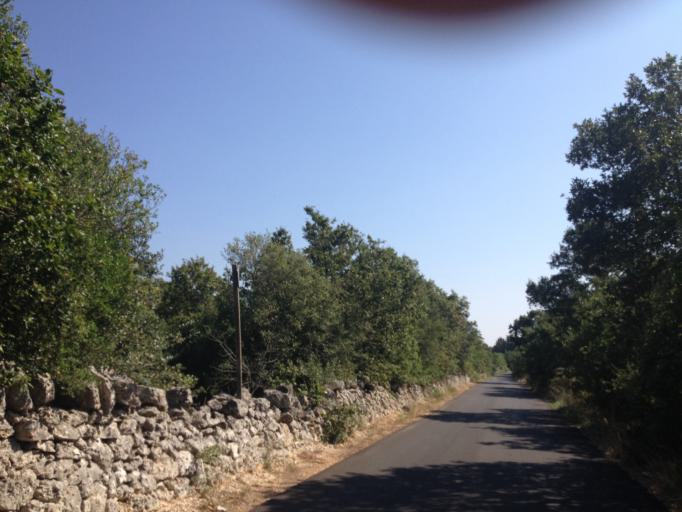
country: IT
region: Apulia
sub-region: Provincia di Bari
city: Alberobello
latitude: 40.8059
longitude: 17.1831
